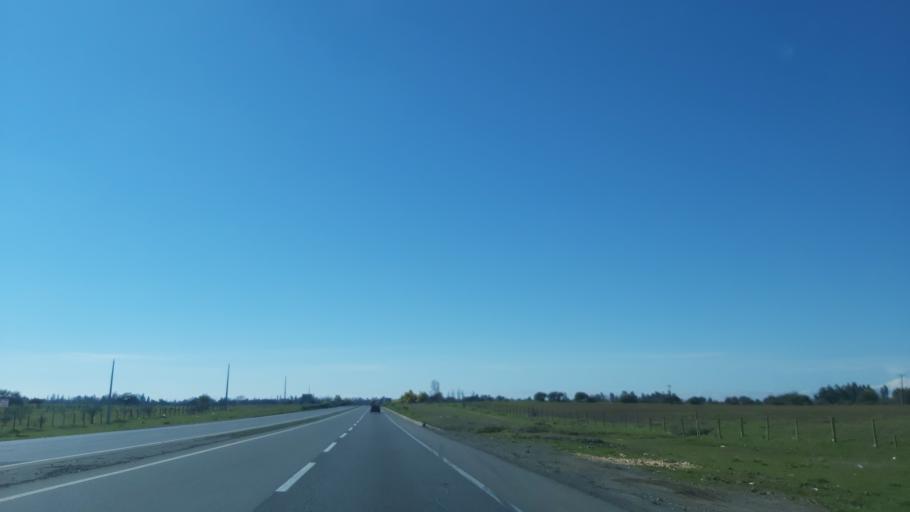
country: CL
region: Biobio
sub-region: Provincia de Nuble
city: Bulnes
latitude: -36.6571
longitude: -72.2473
